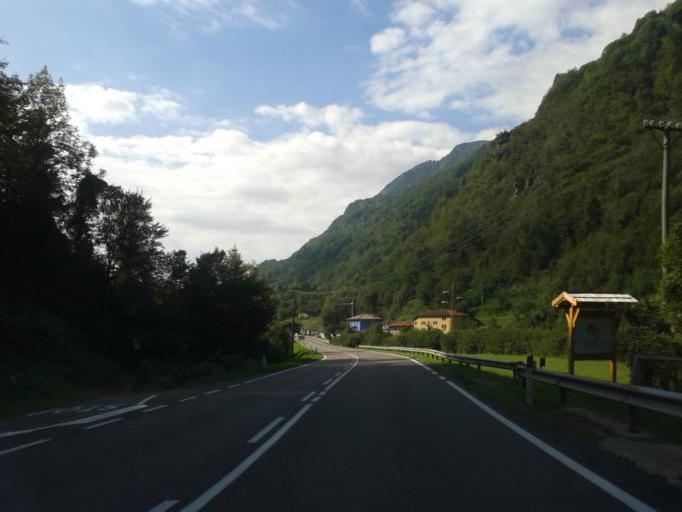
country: IT
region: Trentino-Alto Adige
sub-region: Provincia di Trento
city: Cimego
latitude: 45.9059
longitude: 10.6110
